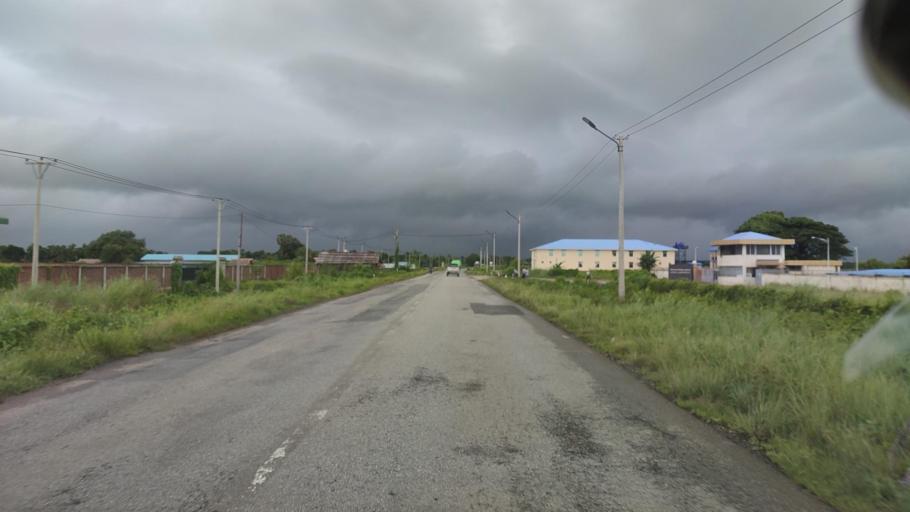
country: MM
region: Bago
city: Bago
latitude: 17.3853
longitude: 96.4890
